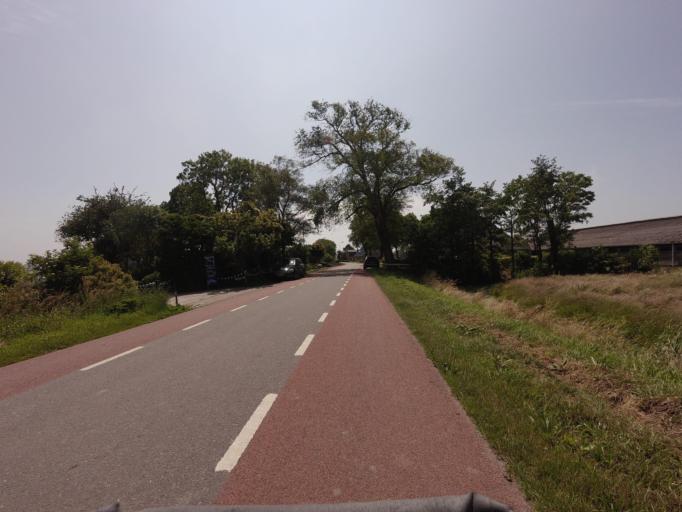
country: NL
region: North Holland
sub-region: Gemeente Opmeer
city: Opmeer
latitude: 52.6874
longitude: 4.9434
